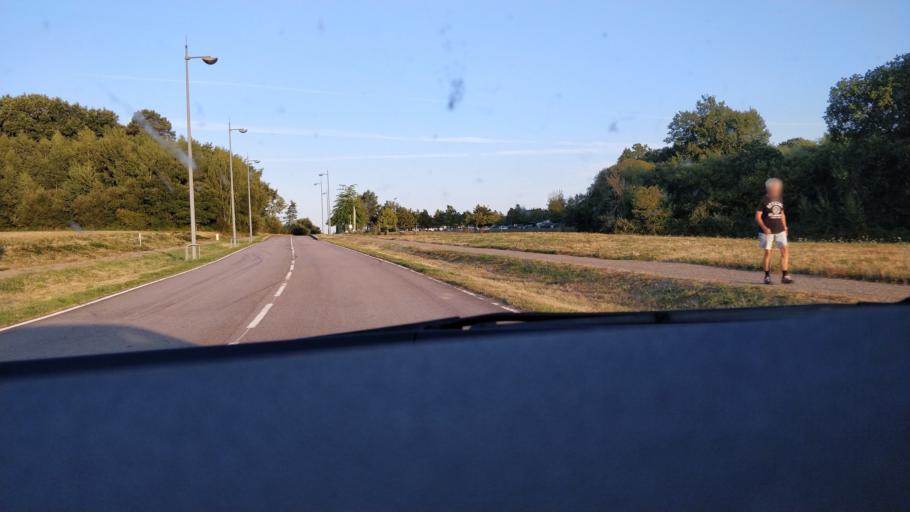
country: FR
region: Limousin
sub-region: Departement de la Haute-Vienne
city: Le Palais-sur-Vienne
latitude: 45.8643
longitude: 1.2983
